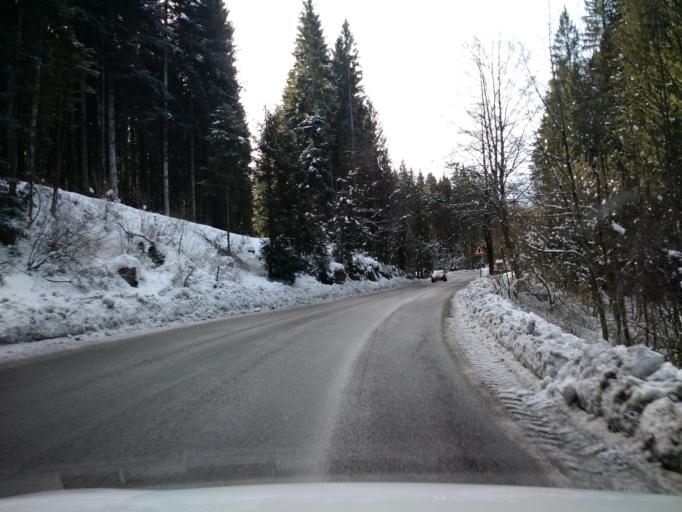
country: IT
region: Veneto
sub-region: Provincia di Vicenza
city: Canove di Roana
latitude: 45.8426
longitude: 11.4667
